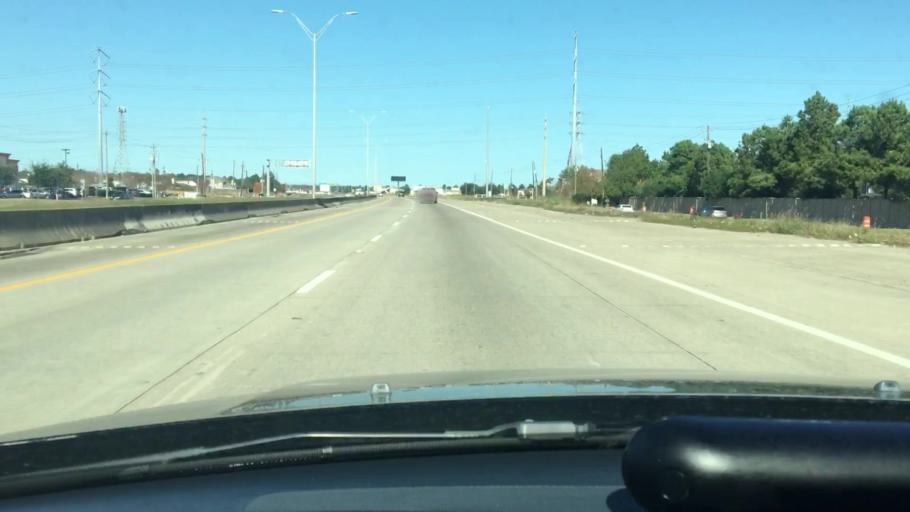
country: US
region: Texas
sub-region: Harris County
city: Cloverleaf
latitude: 29.8152
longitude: -95.1640
